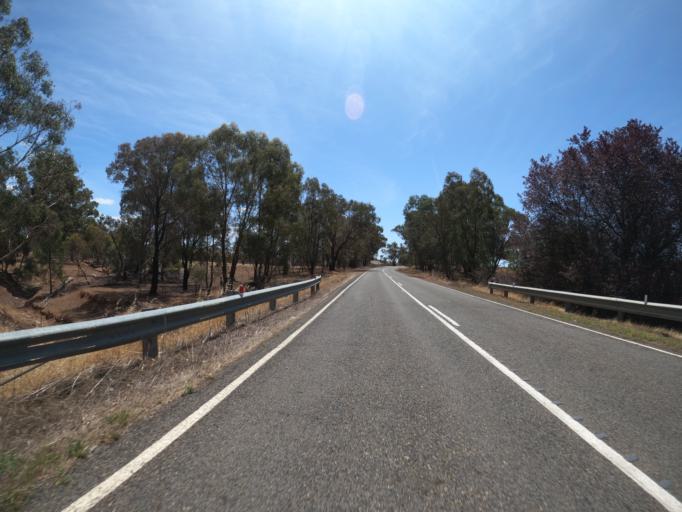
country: AU
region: Victoria
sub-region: Benalla
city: Benalla
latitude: -36.3442
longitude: 145.9597
